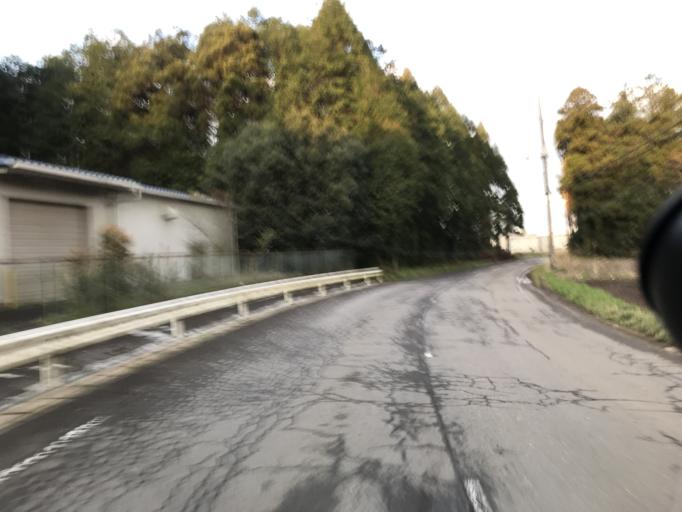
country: JP
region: Chiba
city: Sawara
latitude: 35.8265
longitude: 140.4781
